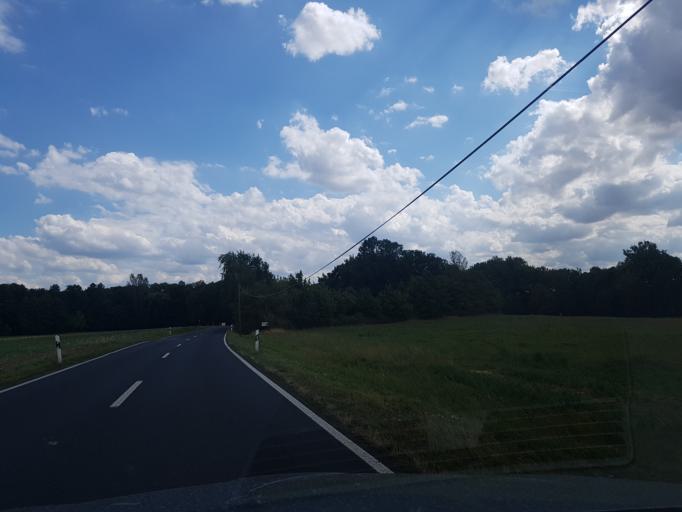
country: DE
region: Saxony
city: Priestewitz
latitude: 51.2573
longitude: 13.5481
